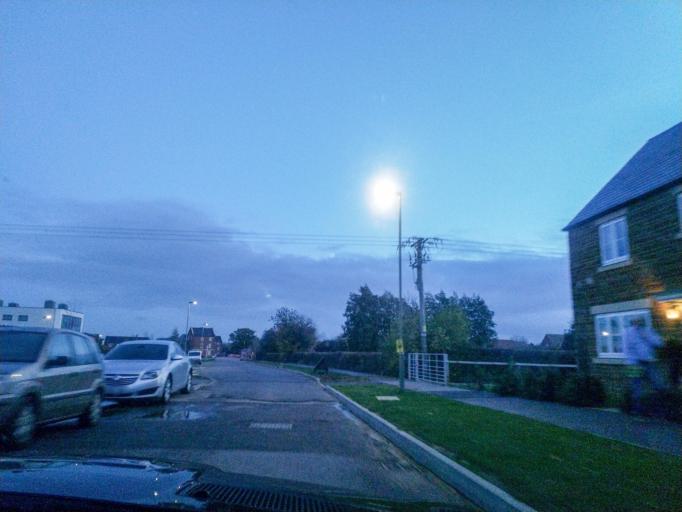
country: GB
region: England
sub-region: Oxfordshire
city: Adderbury
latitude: 52.0411
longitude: -1.3207
